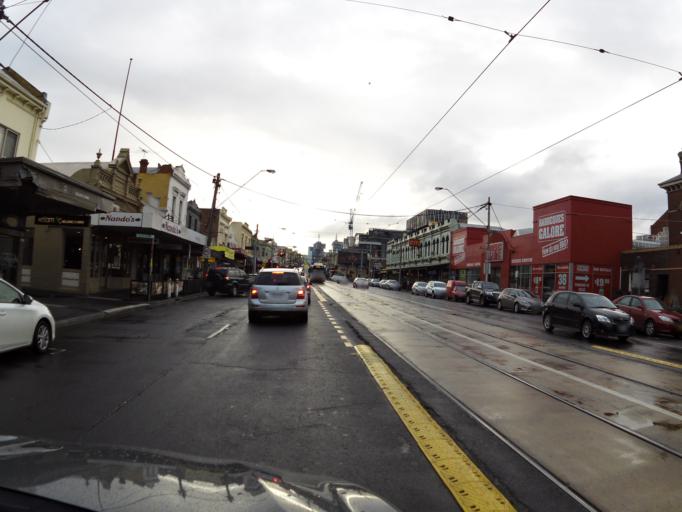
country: AU
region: Victoria
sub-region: Yarra
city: Richmond
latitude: -37.8187
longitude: 145.0006
